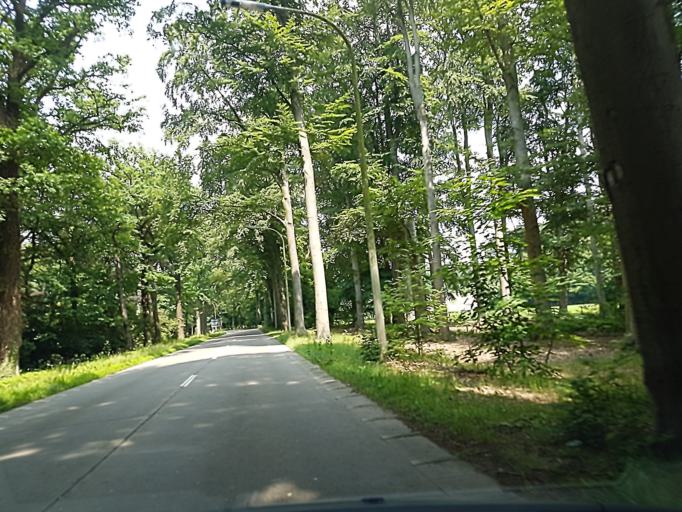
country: BE
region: Flanders
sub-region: Provincie Antwerpen
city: Wijnegem
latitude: 51.2353
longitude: 4.5360
